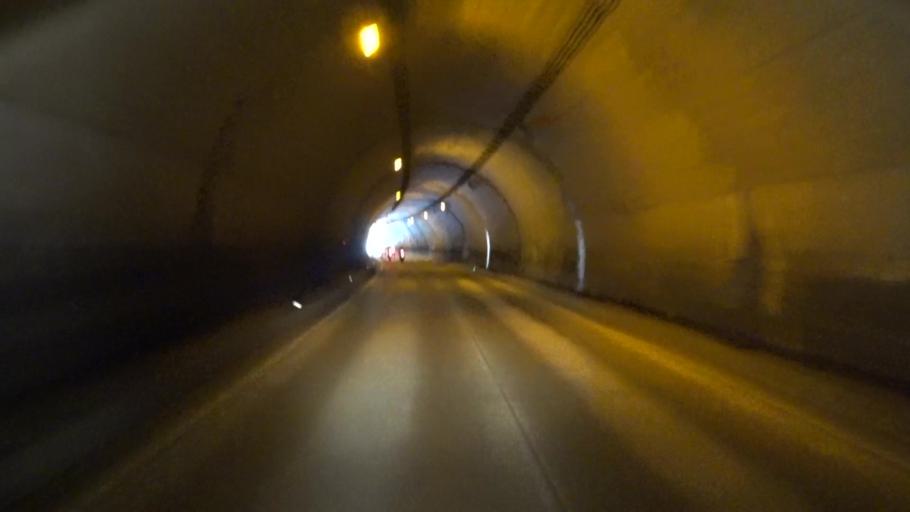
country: JP
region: Shiga Prefecture
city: Kitahama
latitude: 35.2137
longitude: 135.8582
